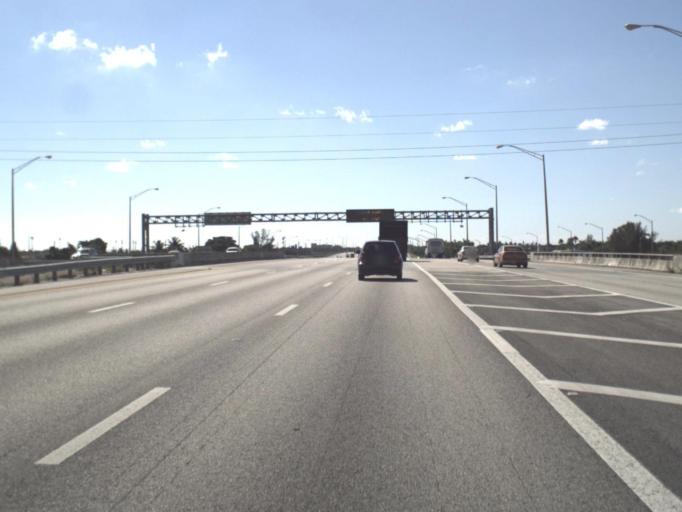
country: US
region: Florida
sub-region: Miami-Dade County
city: Sweetwater
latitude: 25.7690
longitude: -80.3858
